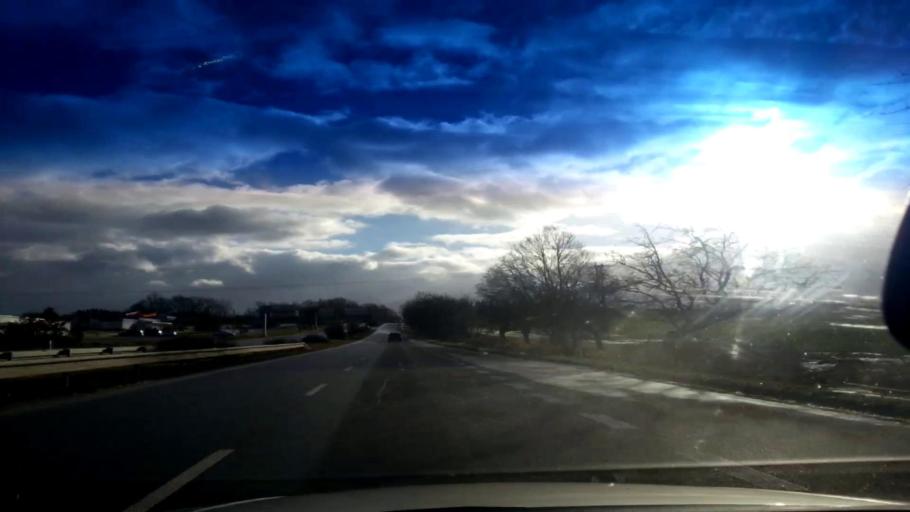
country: CZ
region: Karlovarsky
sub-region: Okres Cheb
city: Cheb
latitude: 50.0957
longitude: 12.3688
